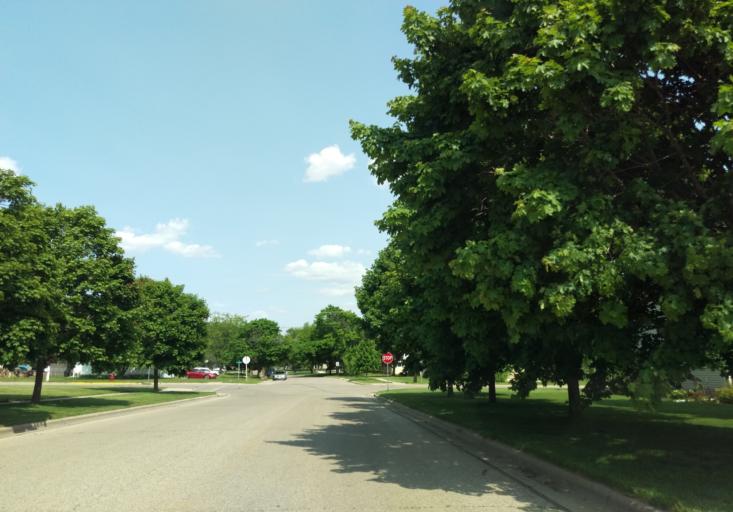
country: US
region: Wisconsin
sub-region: Rock County
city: Evansville
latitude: 42.7750
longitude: -89.3144
